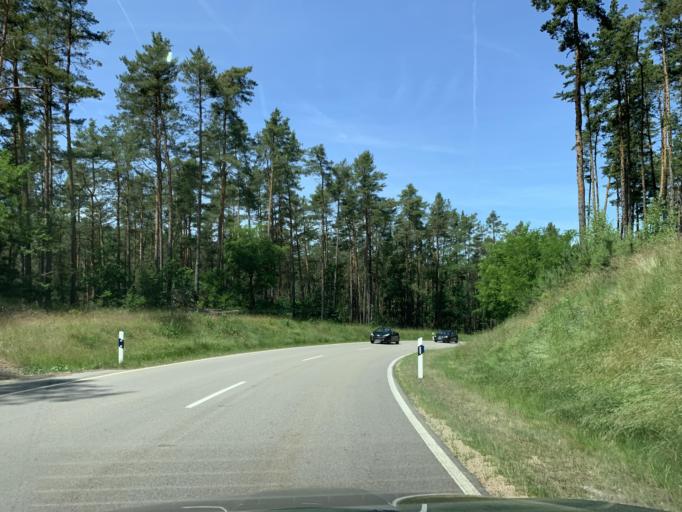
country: DE
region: Bavaria
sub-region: Upper Palatinate
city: Schwarzhofen
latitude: 49.3713
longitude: 12.3286
